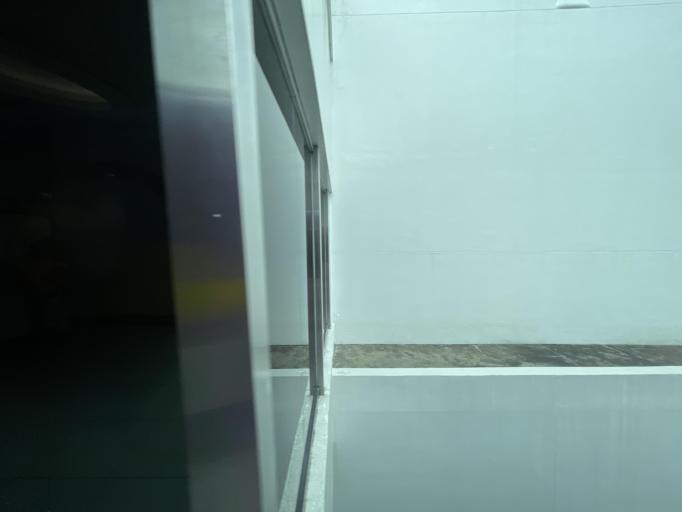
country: SG
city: Singapore
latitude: 1.2651
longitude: 103.8225
